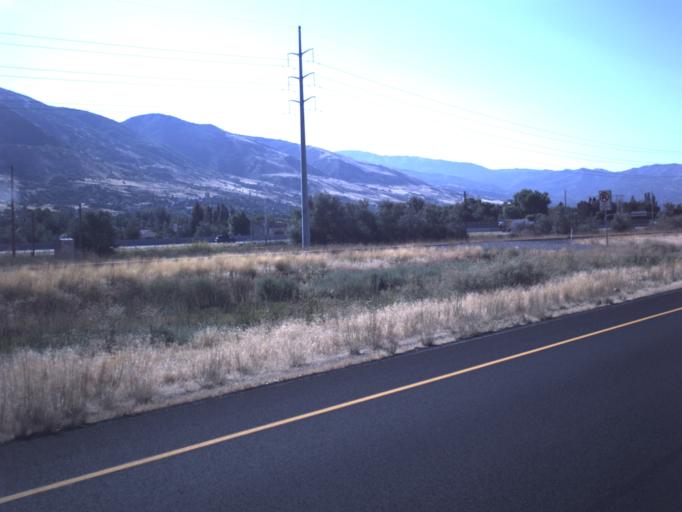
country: US
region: Utah
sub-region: Davis County
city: Farmington
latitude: 40.9509
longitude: -111.8932
